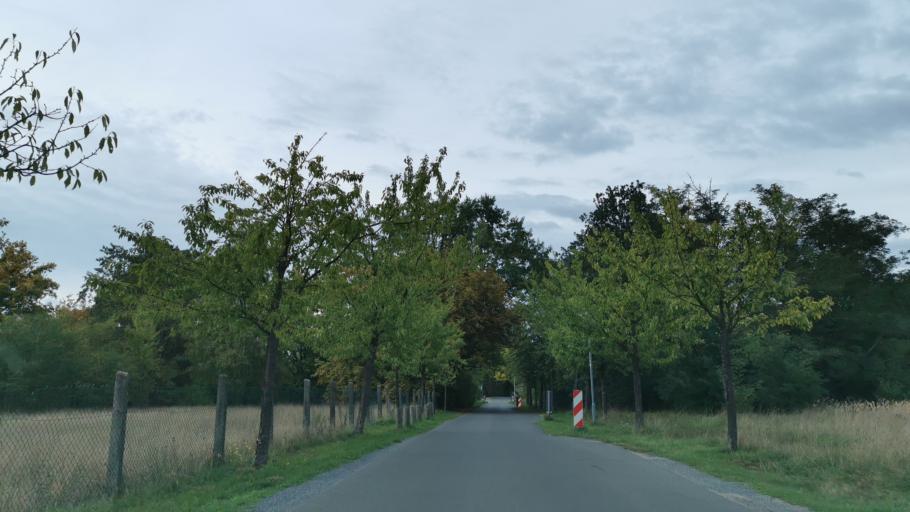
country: DE
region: Brandenburg
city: Werder
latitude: 52.3588
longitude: 12.9479
